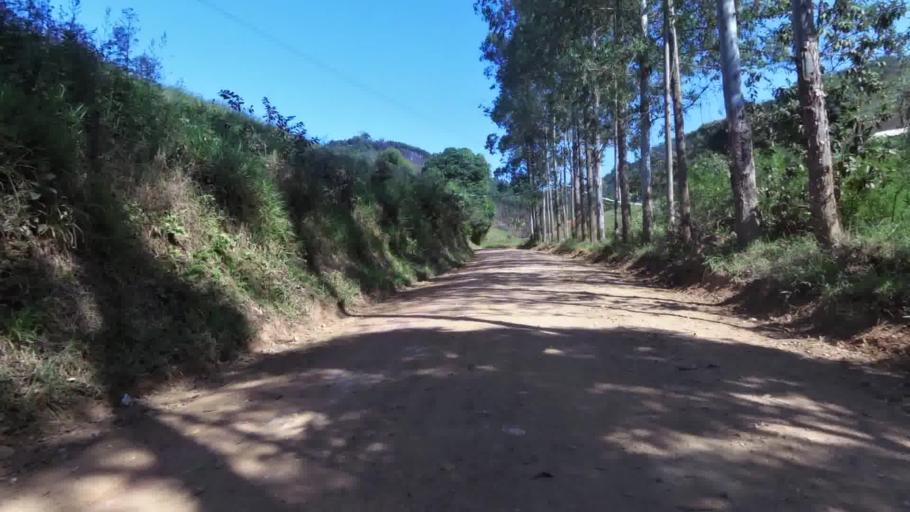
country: BR
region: Espirito Santo
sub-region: Alfredo Chaves
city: Alfredo Chaves
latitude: -20.5322
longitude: -40.8444
